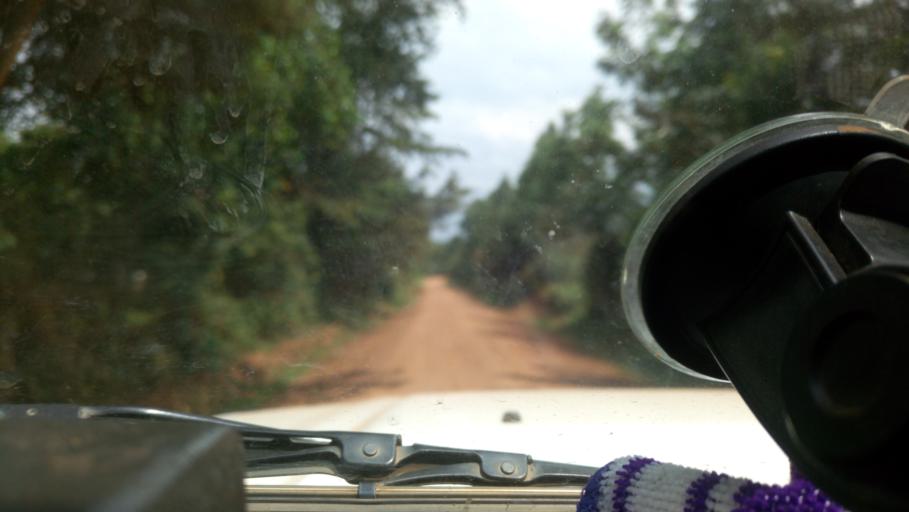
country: KE
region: Kericho
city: Sotik
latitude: -0.6213
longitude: 35.1124
